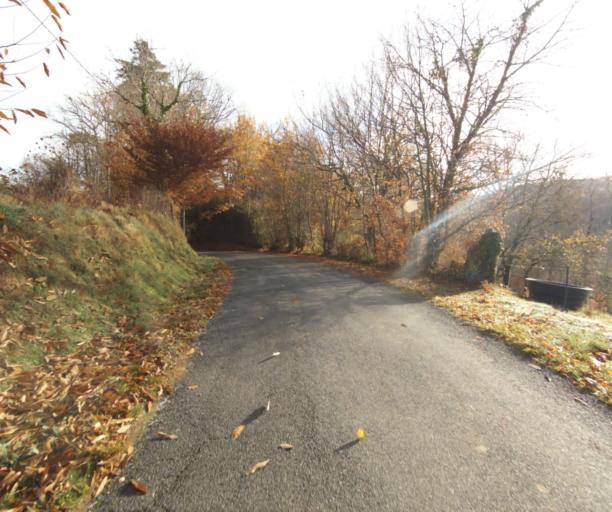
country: FR
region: Limousin
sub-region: Departement de la Correze
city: Chameyrat
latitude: 45.2273
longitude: 1.7243
